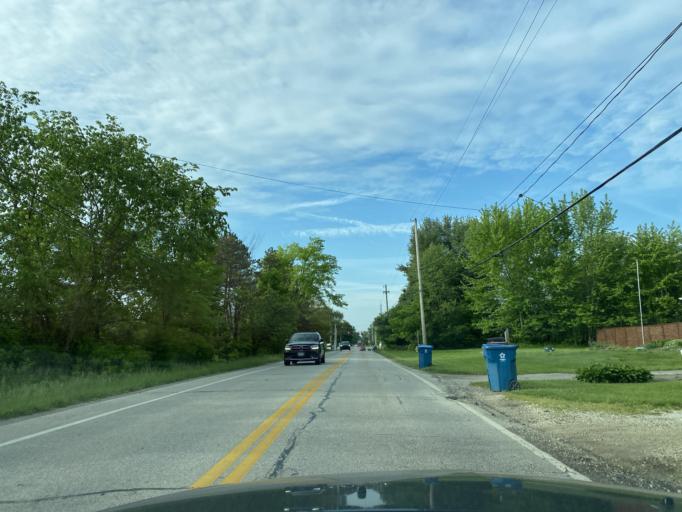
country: US
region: Ohio
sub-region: Summit County
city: Fairlawn
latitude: 41.0951
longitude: -81.6194
